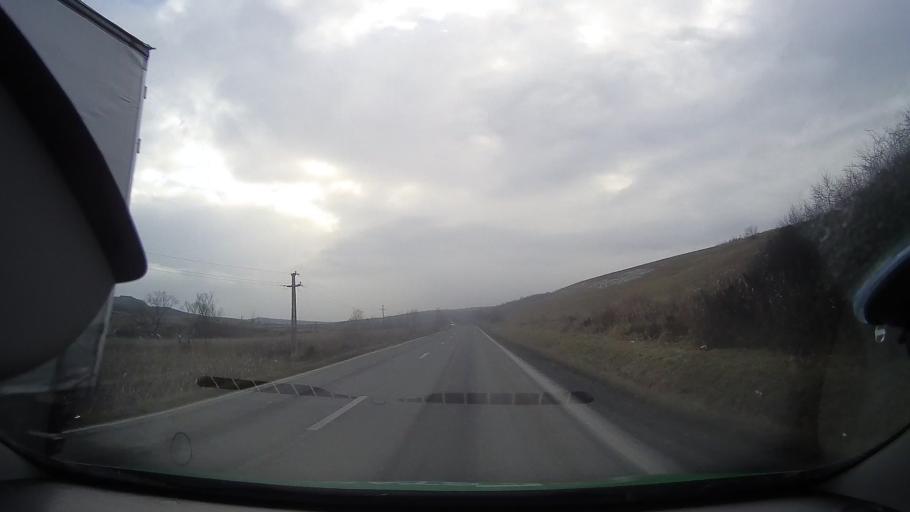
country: RO
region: Mures
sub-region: Comuna Cucerdea
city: Cucerdea
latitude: 46.3940
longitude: 24.2582
